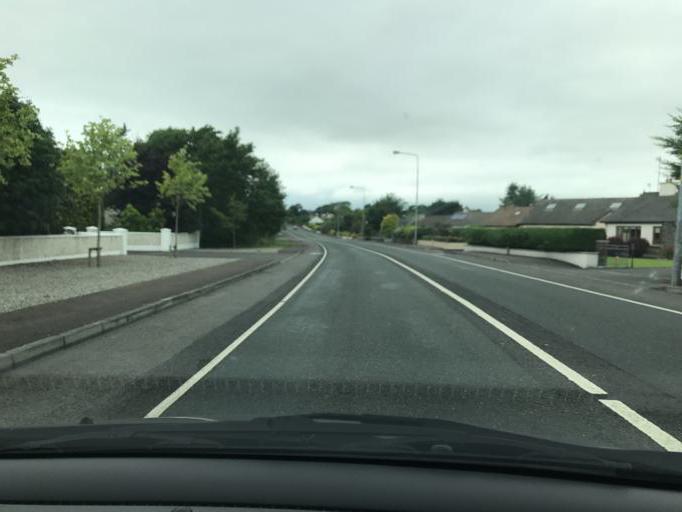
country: IE
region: Connaught
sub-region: Sligo
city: Sligo
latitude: 54.2950
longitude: -8.4928
